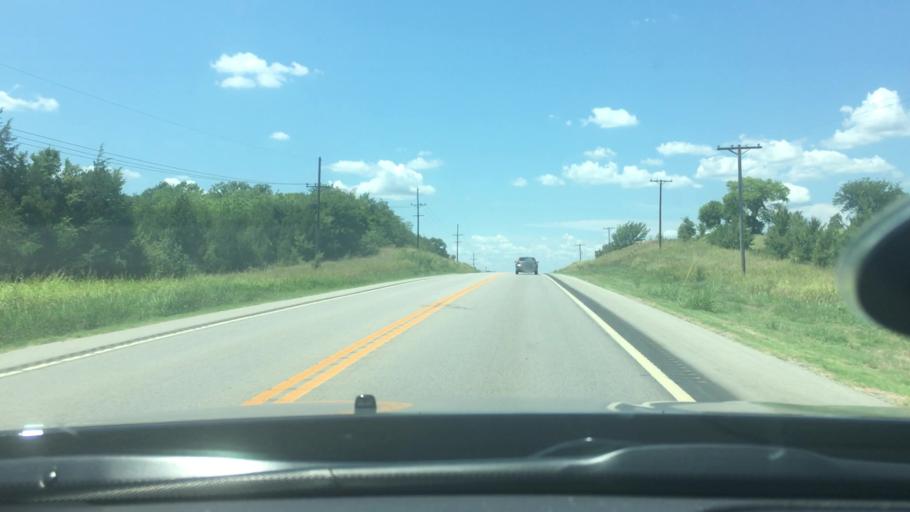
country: US
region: Oklahoma
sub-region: Bryan County
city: Durant
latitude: 33.9975
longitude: -96.2915
